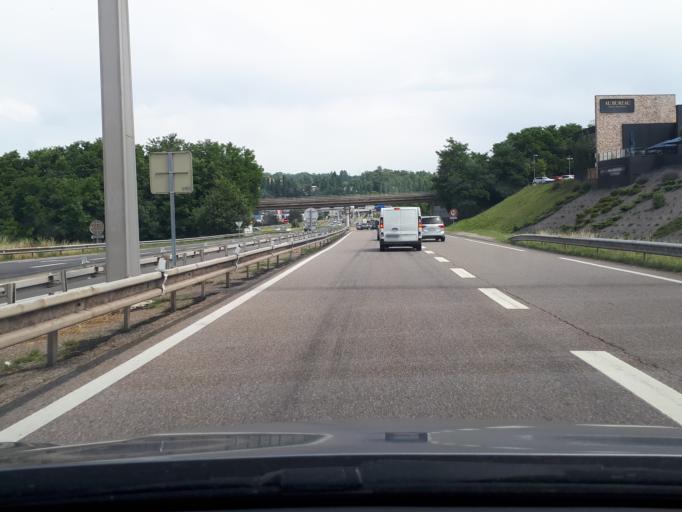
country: FR
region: Rhone-Alpes
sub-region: Departement de la Loire
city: Villars
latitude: 45.4770
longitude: 4.3465
